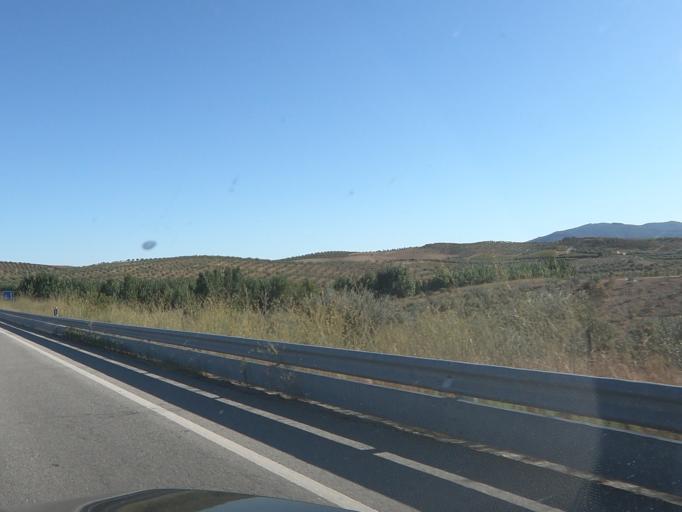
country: PT
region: Vila Real
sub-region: Valpacos
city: Valpacos
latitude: 41.5603
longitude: -7.2653
